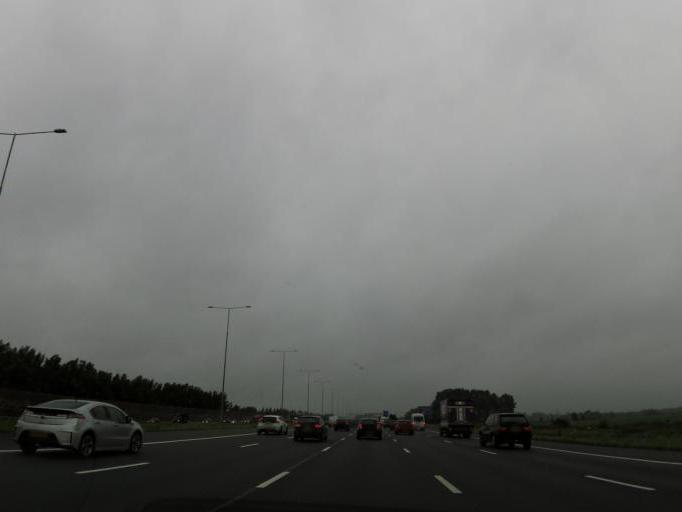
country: NL
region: North Holland
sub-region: Gemeente Amsterdam
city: Amsterdam-Zuidoost
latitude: 52.2495
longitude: 4.9698
